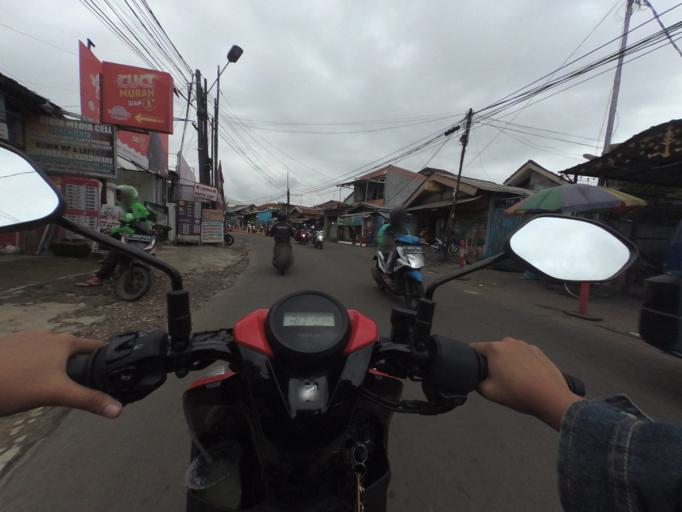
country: ID
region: West Java
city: Bogor
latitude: -6.5690
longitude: 106.7994
